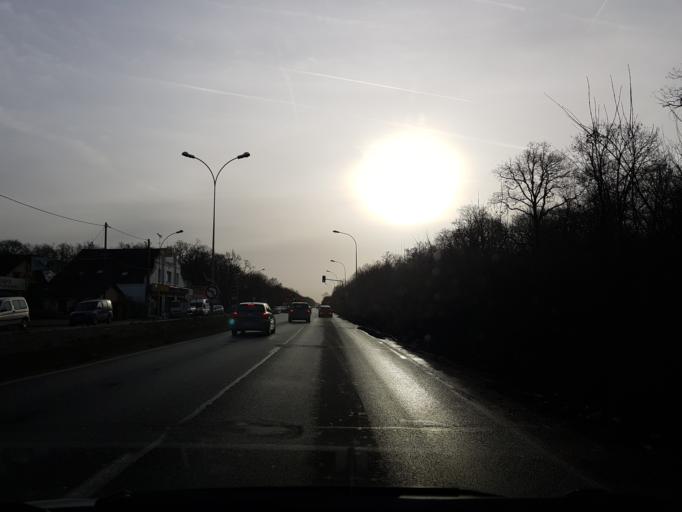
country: FR
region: Ile-de-France
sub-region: Departement de l'Essonne
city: Brunoy
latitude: 48.6791
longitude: 2.4952
